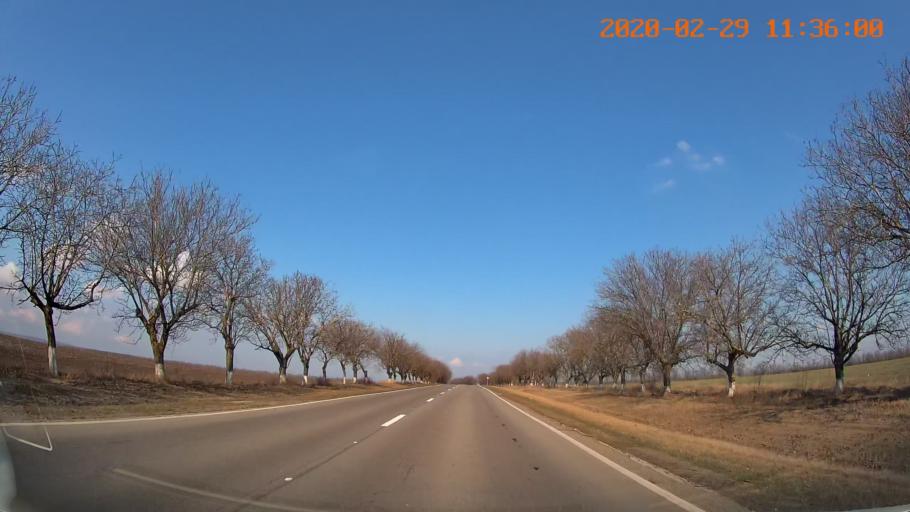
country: MD
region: Rezina
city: Saharna
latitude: 47.5892
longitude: 29.0595
